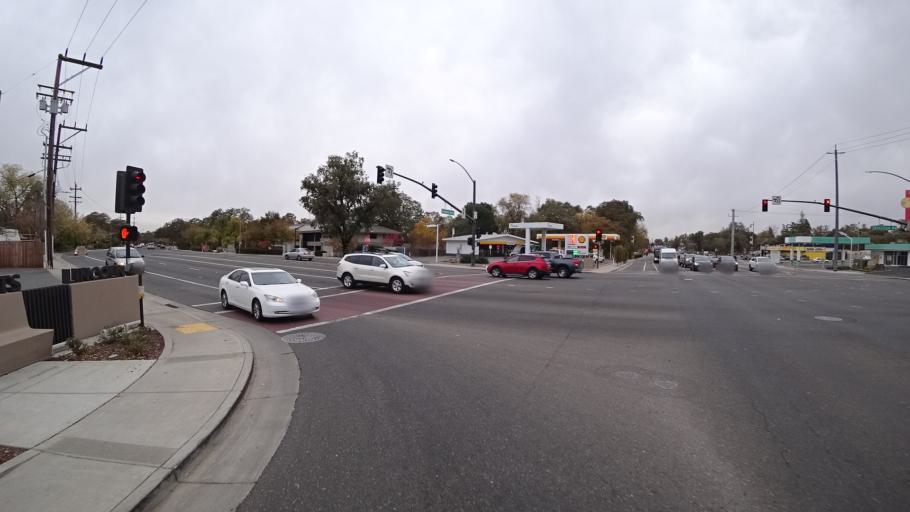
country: US
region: California
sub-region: Sacramento County
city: Citrus Heights
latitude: 38.7064
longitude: -121.2906
